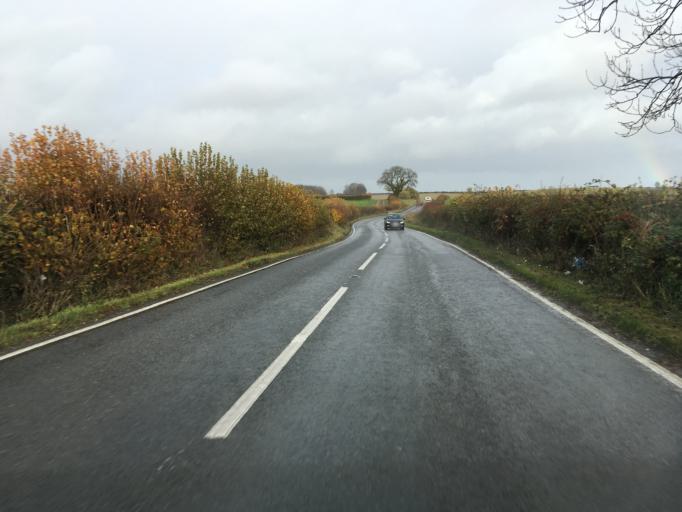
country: GB
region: England
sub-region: South Gloucestershire
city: Cold Ashton
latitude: 51.4615
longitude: -2.3754
